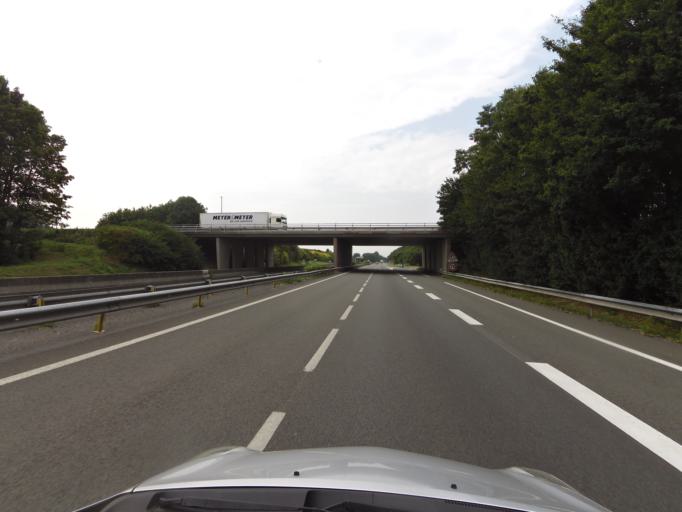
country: FR
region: Nord-Pas-de-Calais
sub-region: Departement du Pas-de-Calais
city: Bourlon
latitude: 50.1439
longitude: 3.1280
